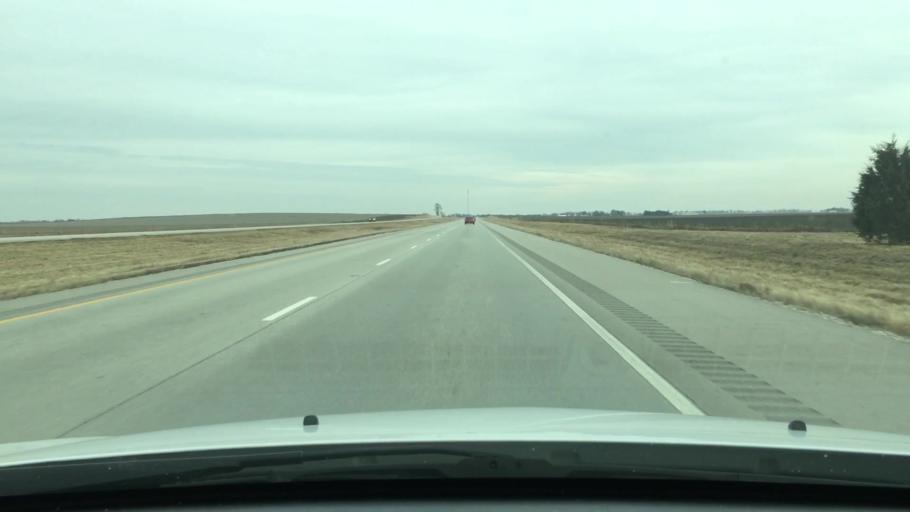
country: US
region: Illinois
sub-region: Morgan County
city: Jacksonville
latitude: 39.7381
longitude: -90.1085
